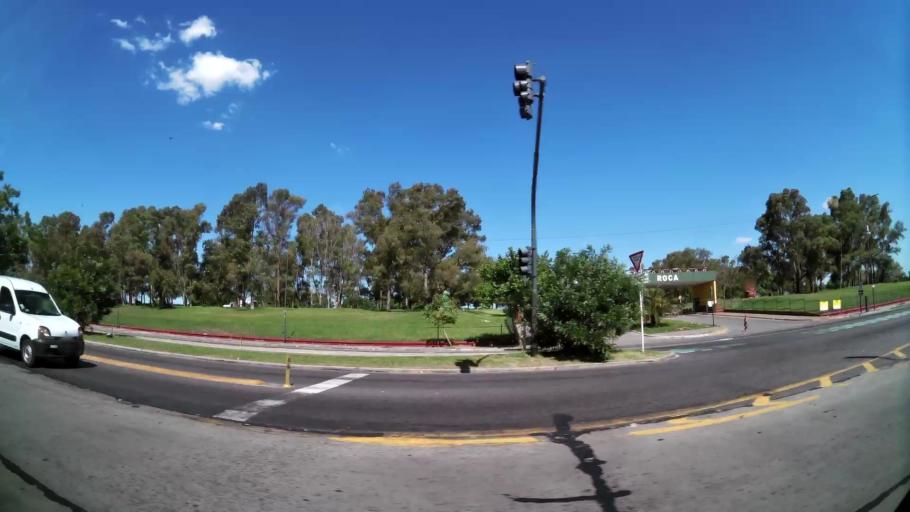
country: AR
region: Buenos Aires F.D.
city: Villa Lugano
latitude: -34.6722
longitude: -58.4458
